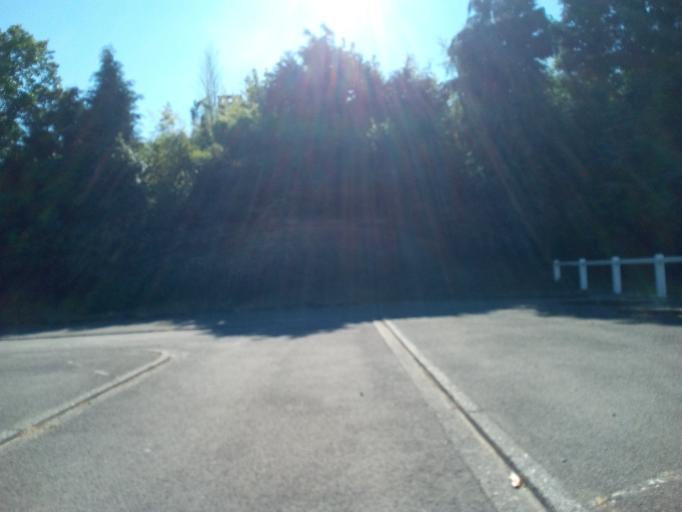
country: FR
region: Brittany
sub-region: Departement du Finistere
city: Landivisiau
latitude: 48.5159
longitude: -4.0743
